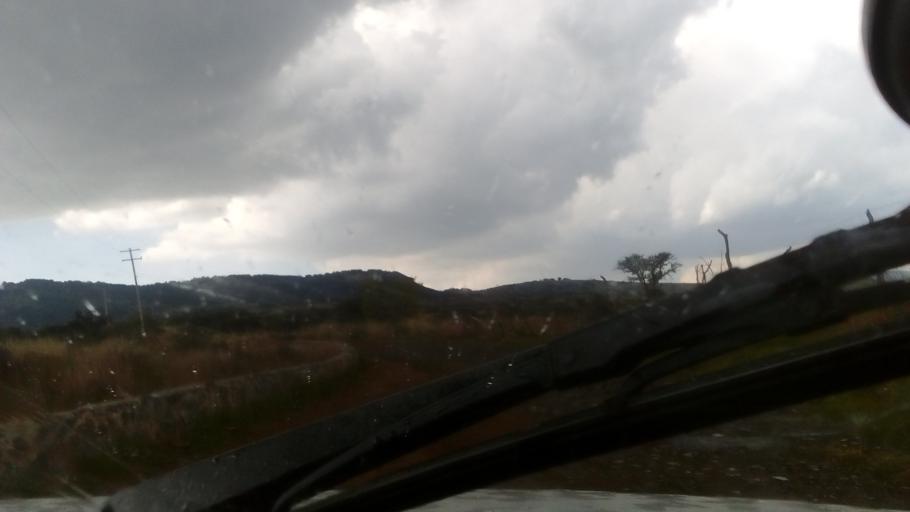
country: MX
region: Guanajuato
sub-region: Silao de la Victoria
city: San Francisco (Banos de Agua Caliente)
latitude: 21.1594
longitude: -101.4225
